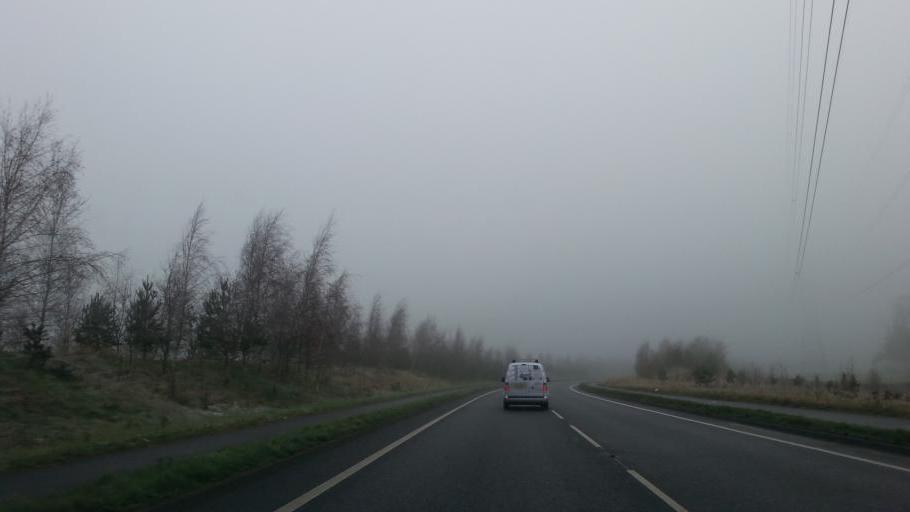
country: GB
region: England
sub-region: Cheshire East
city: Alderley Edge
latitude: 53.2890
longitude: -2.2537
